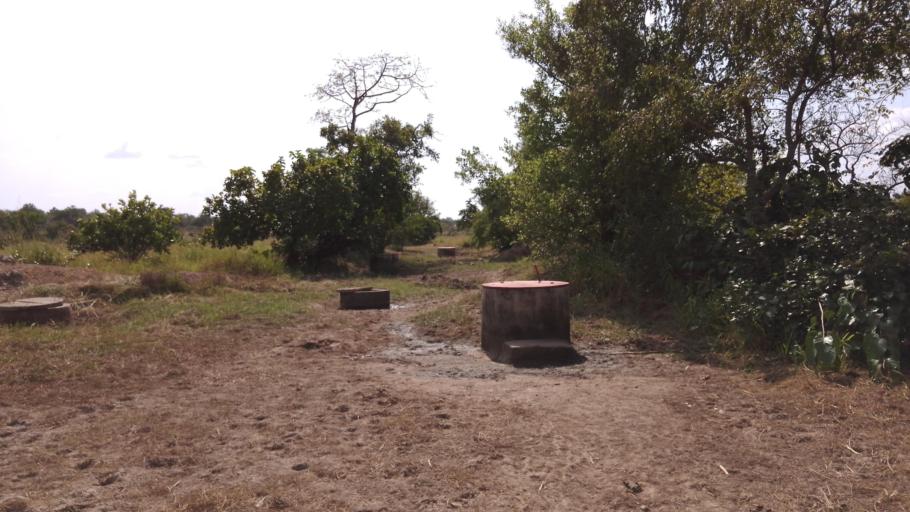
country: GH
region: Northern
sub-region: Yendi
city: Yendi
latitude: 9.7487
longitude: 0.4324
